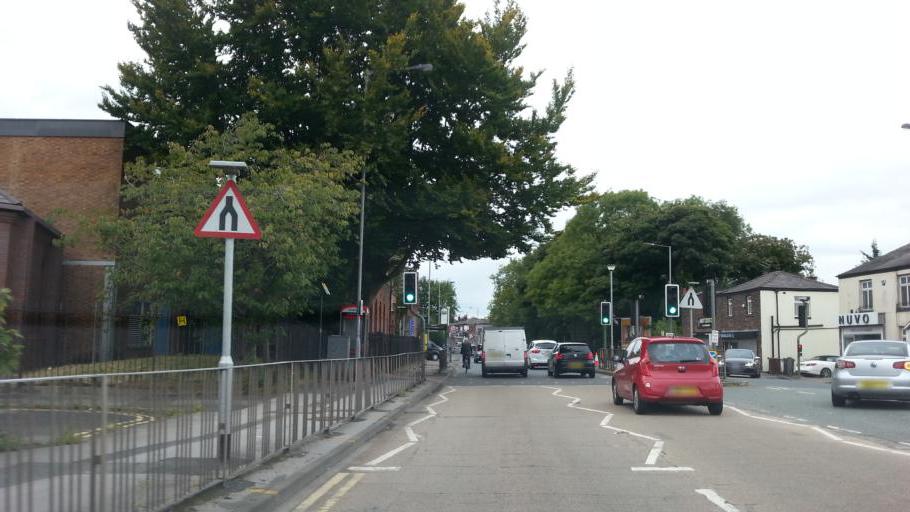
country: GB
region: England
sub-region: Borough of Bury
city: Whitefield
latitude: 53.5446
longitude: -2.2912
